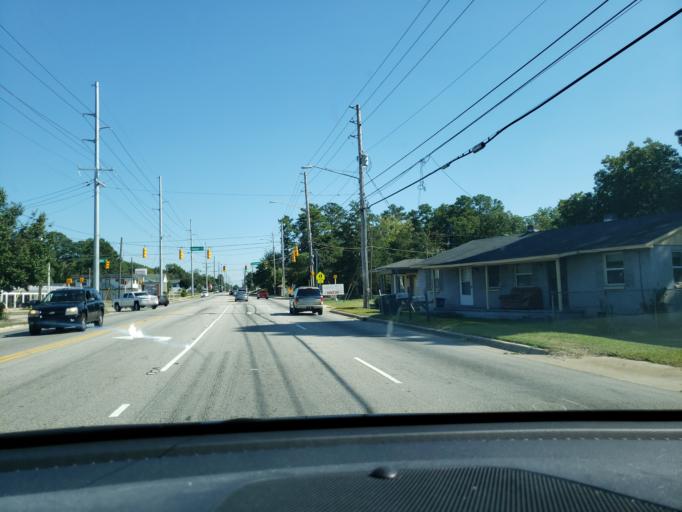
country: US
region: North Carolina
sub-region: Cumberland County
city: Fayetteville
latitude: 35.0852
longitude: -78.9054
